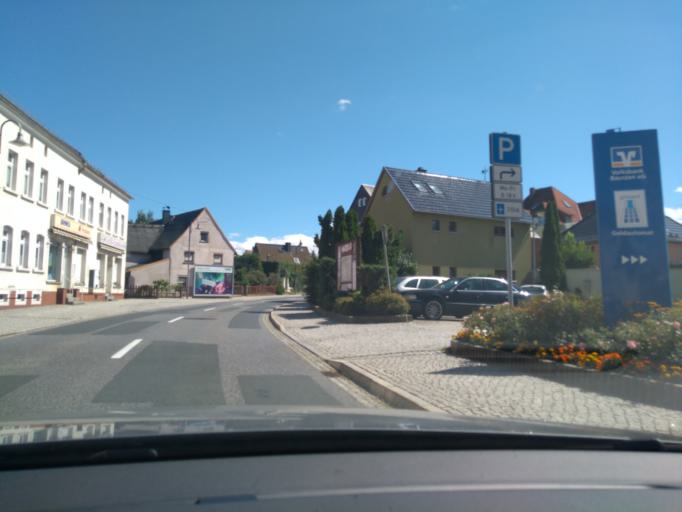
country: DE
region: Saxony
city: Grossrohrsdorf
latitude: 51.1462
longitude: 14.0261
